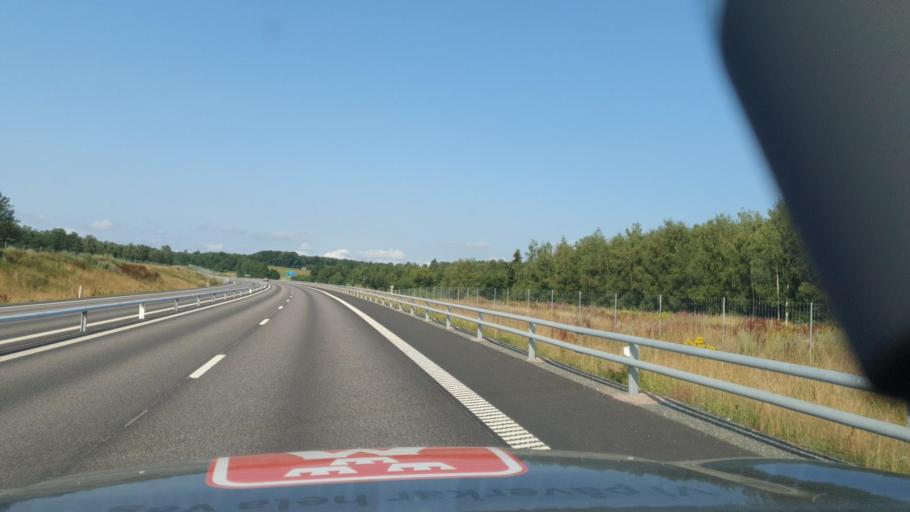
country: SE
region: Skane
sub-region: Hassleholms Kommun
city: Vinslov
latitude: 55.9455
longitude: 13.8737
